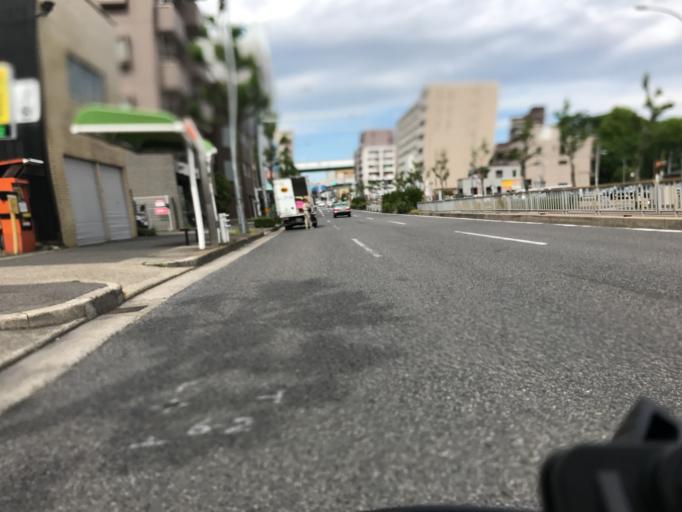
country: JP
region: Aichi
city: Nagoya-shi
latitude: 35.1788
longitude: 136.9177
